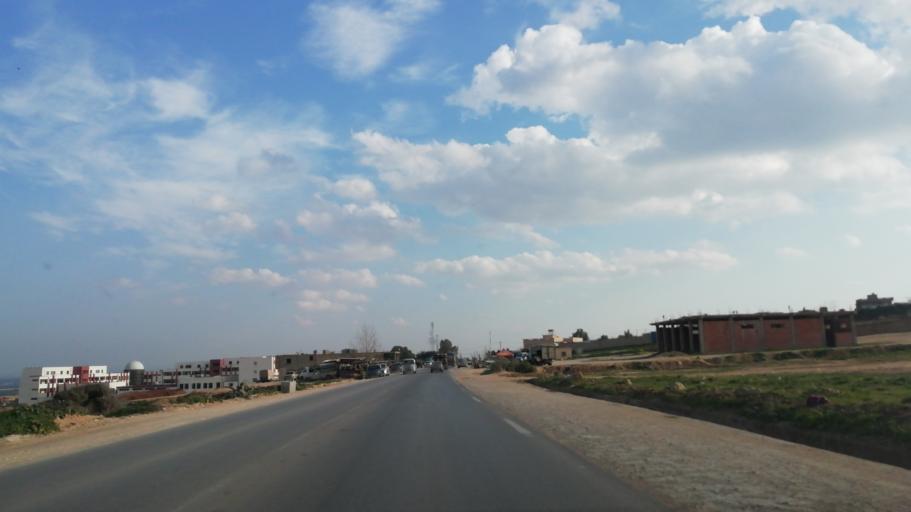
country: DZ
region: Relizane
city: Relizane
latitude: 35.9127
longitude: 0.5020
